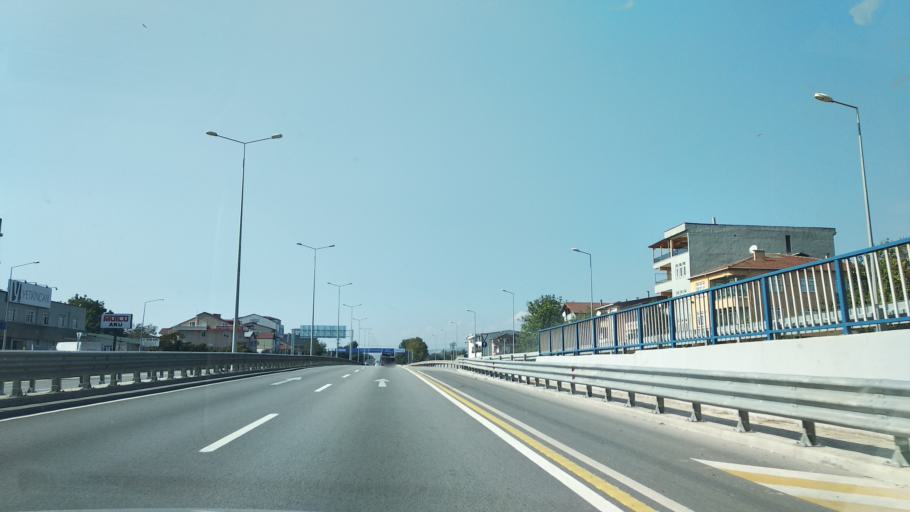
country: TR
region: Kocaeli
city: Kosekoy
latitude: 40.7539
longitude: 30.0206
